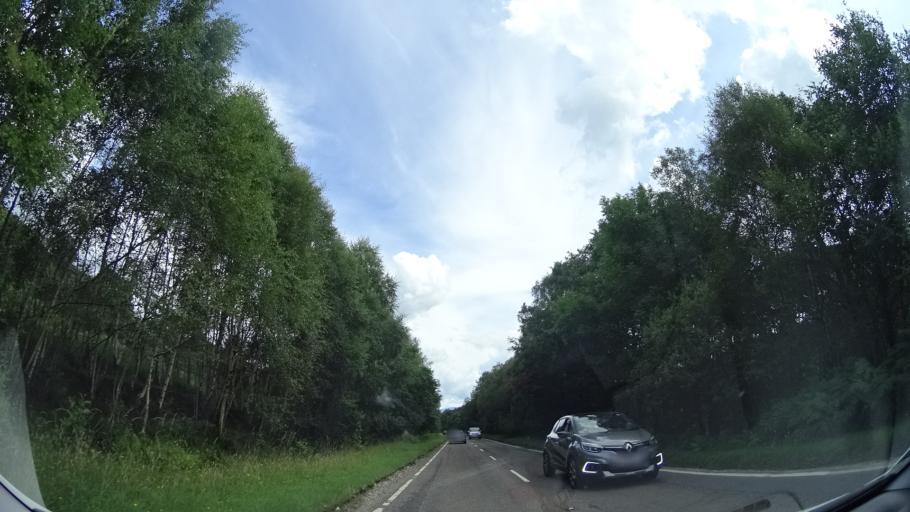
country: GB
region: Scotland
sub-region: Highland
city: Fort William
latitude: 56.8568
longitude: -5.3050
